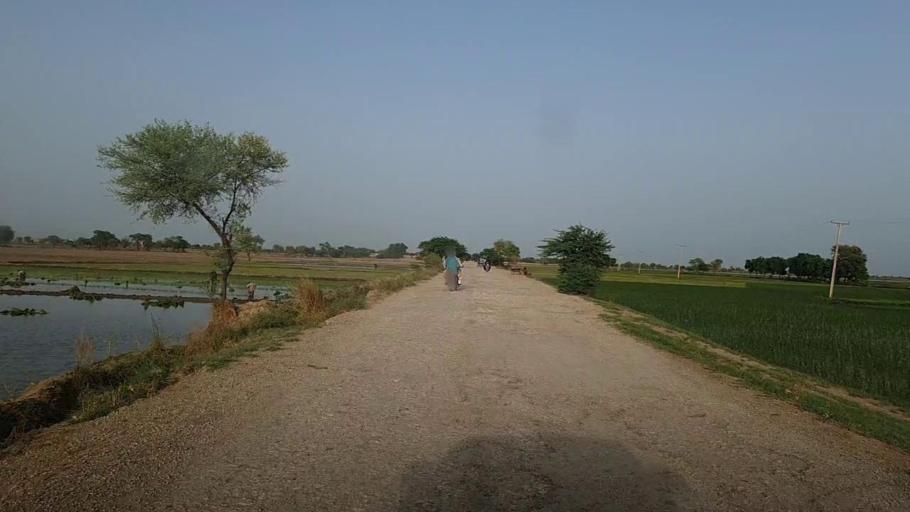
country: PK
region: Sindh
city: Mehar
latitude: 27.1646
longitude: 67.7827
